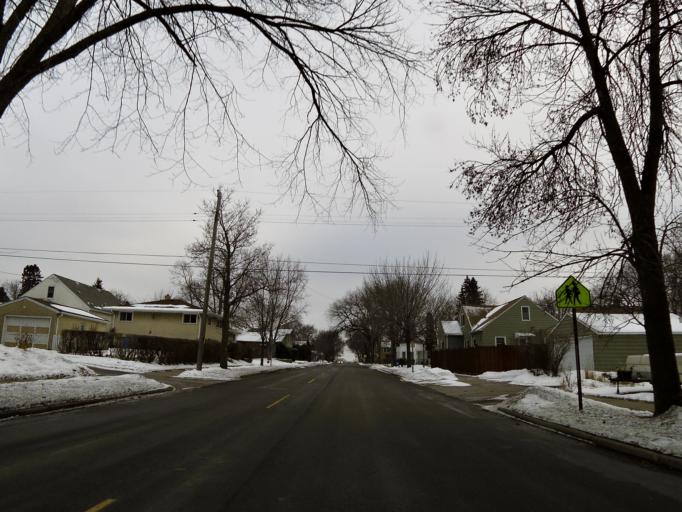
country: US
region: Minnesota
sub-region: Dakota County
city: Mendota Heights
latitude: 44.9214
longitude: -93.1925
